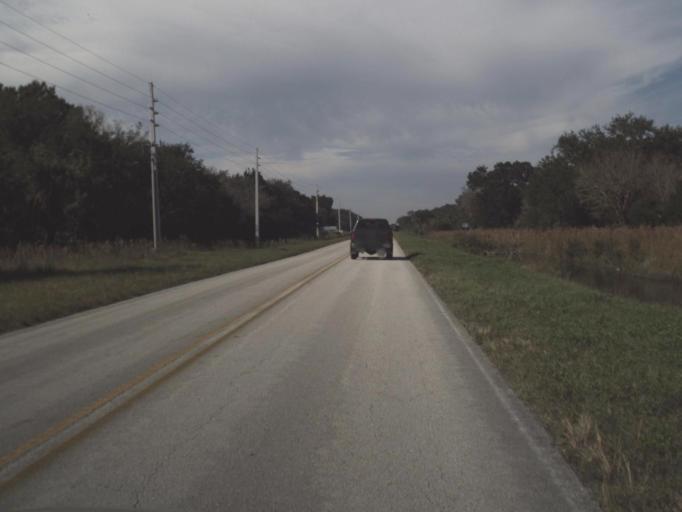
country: US
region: Florida
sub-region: Brevard County
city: Titusville
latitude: 28.6436
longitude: -80.7341
